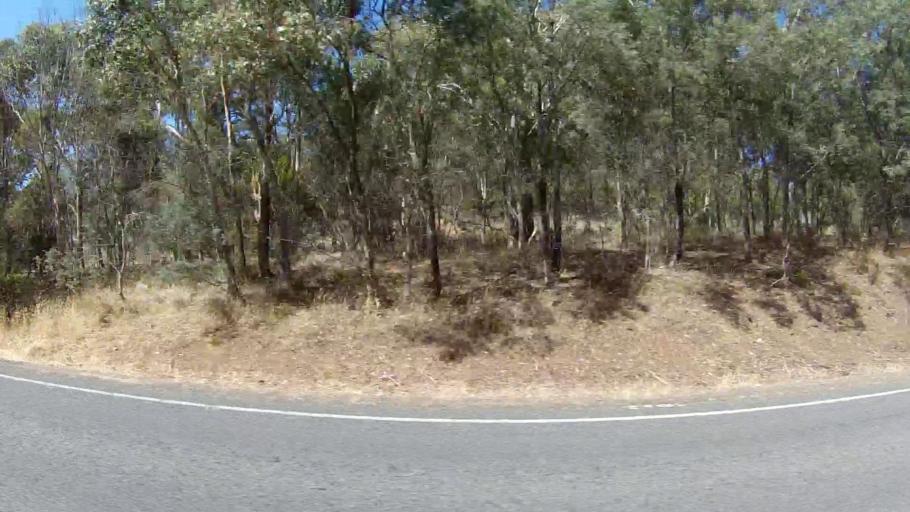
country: AU
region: Tasmania
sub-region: Sorell
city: Sorell
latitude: -42.6079
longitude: 147.6706
